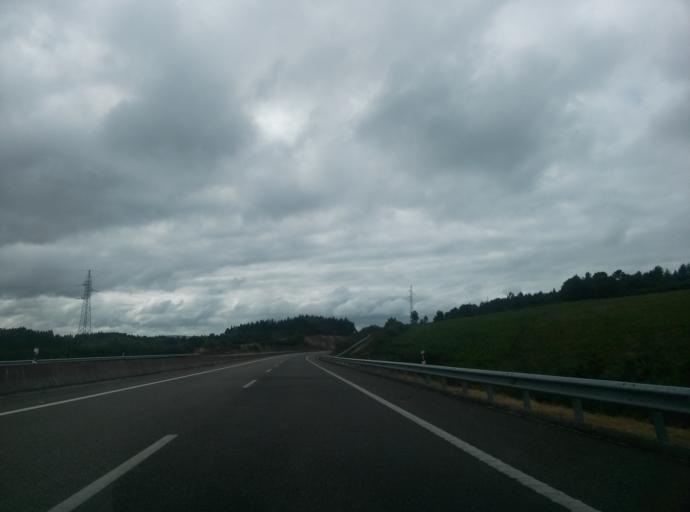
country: ES
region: Galicia
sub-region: Provincia de Lugo
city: Vilalba
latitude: 43.3451
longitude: -7.7233
